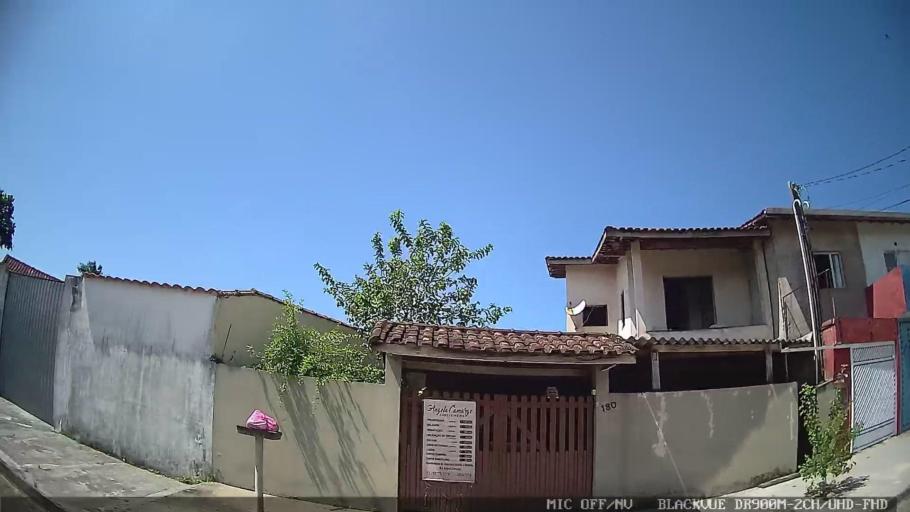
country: BR
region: Sao Paulo
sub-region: Peruibe
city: Peruibe
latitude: -24.3061
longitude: -46.9971
